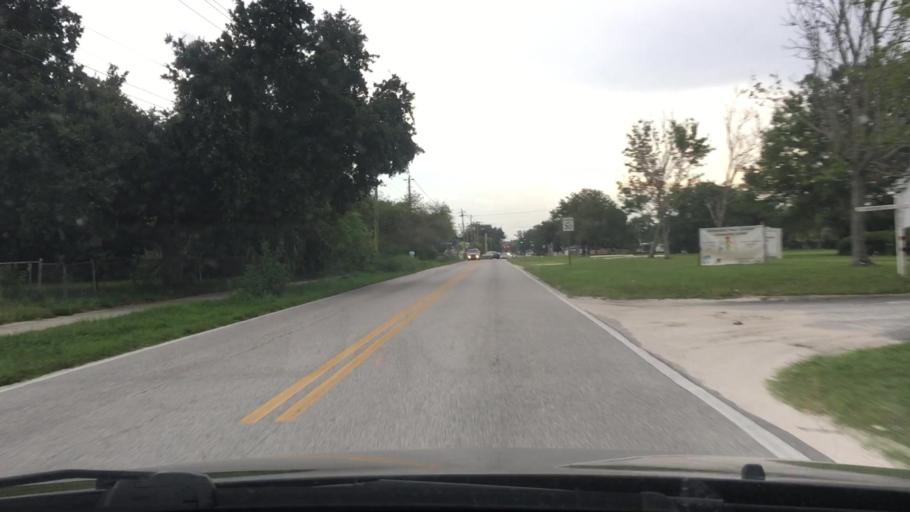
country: US
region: Florida
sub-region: Volusia County
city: Holly Hill
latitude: 29.2315
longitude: -81.0639
